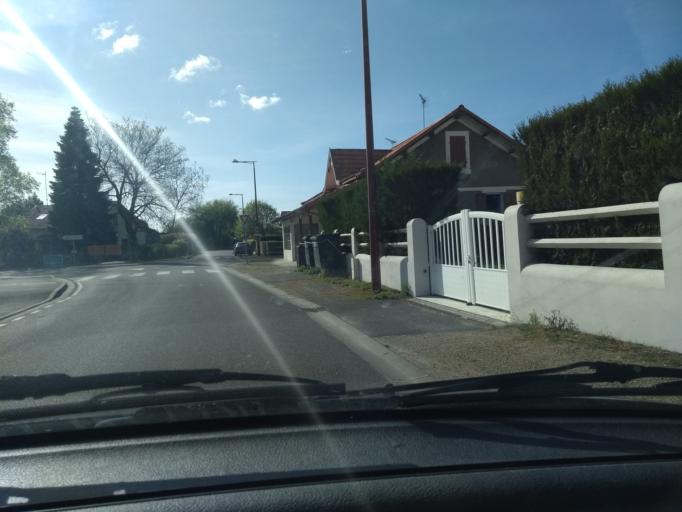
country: FR
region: Aquitaine
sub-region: Departement des Landes
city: Parentis-en-Born
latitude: 44.3495
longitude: -1.0808
